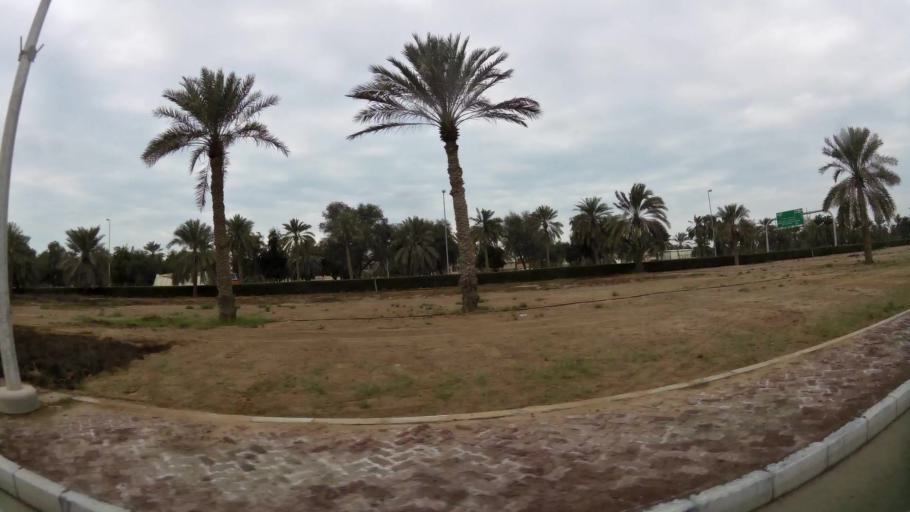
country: AE
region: Abu Dhabi
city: Abu Dhabi
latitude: 24.4324
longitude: 54.3754
